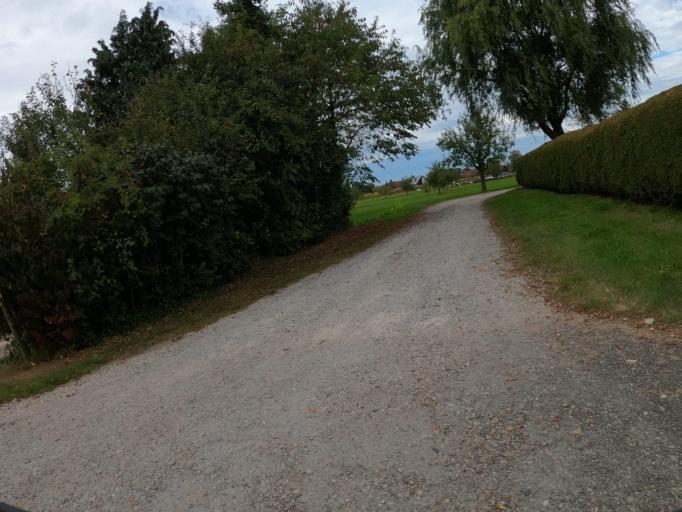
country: DE
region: Bavaria
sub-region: Swabia
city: Holzheim
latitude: 48.3804
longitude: 10.0737
